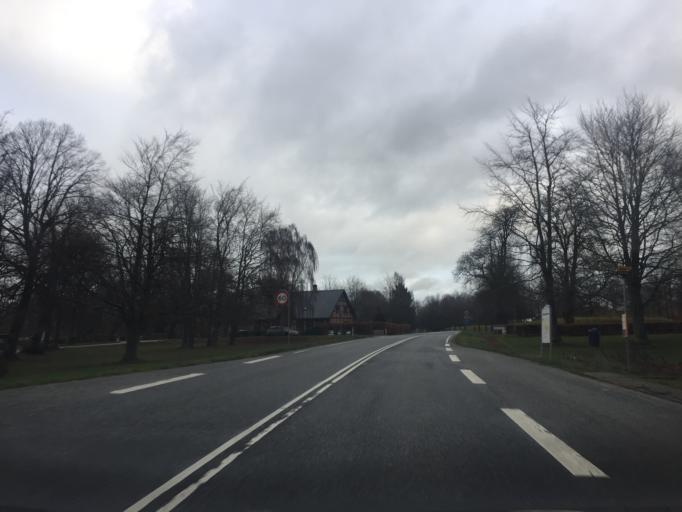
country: DK
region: Zealand
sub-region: Holbaek Kommune
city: Tollose
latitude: 55.6127
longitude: 11.7431
